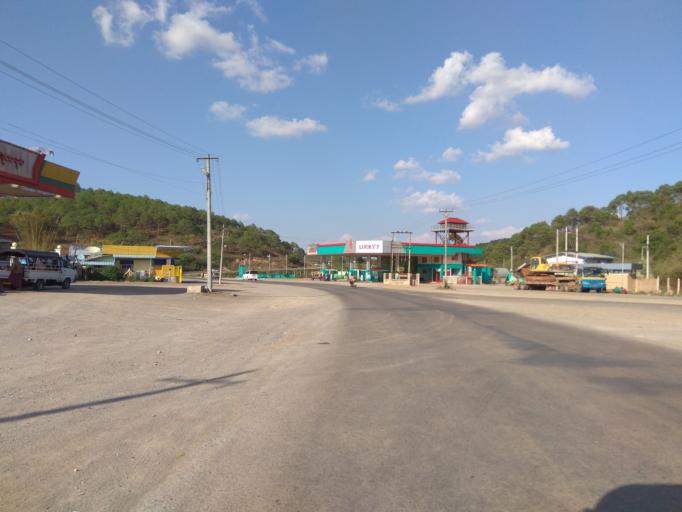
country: MM
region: Shan
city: Taunggyi
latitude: 20.6440
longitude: 96.6084
